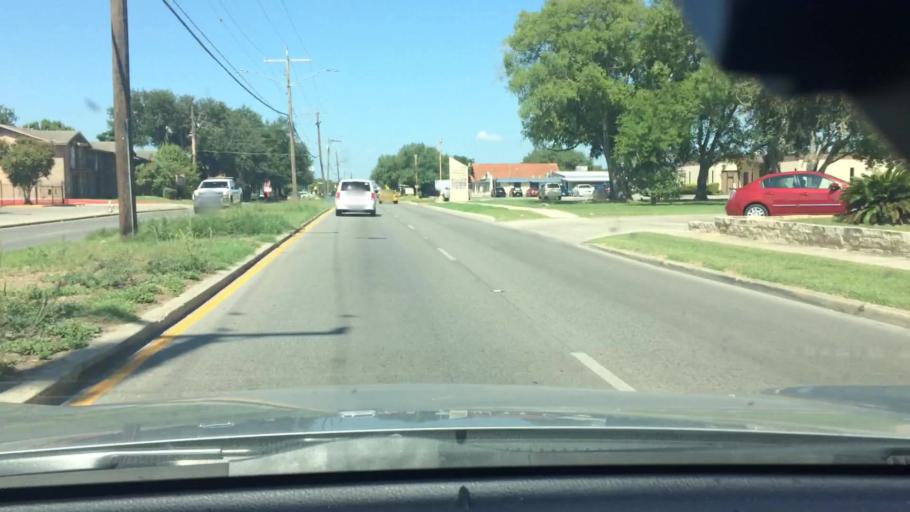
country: US
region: Texas
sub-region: Bexar County
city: China Grove
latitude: 29.3748
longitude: -98.4131
